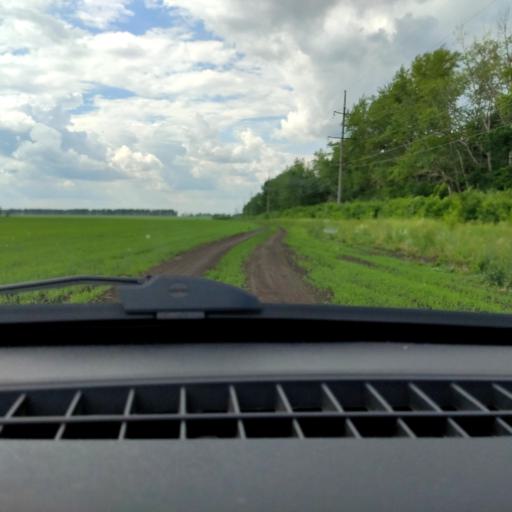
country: RU
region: Bashkortostan
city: Kabakovo
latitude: 54.5192
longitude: 56.0796
